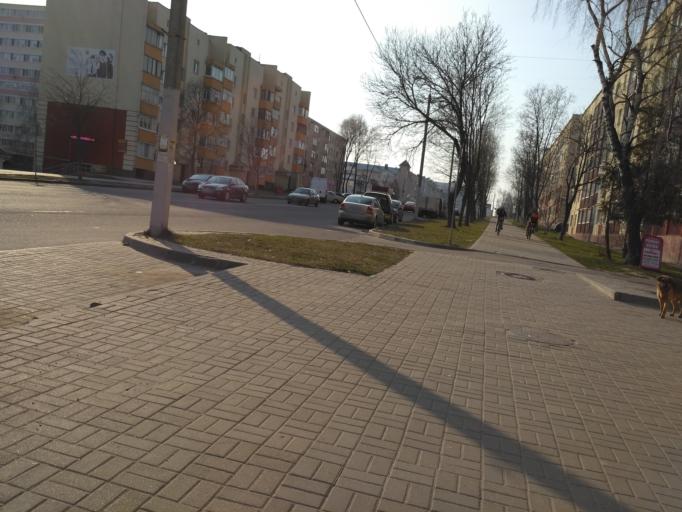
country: BY
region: Minsk
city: Zaslawye
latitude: 54.0114
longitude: 27.2683
